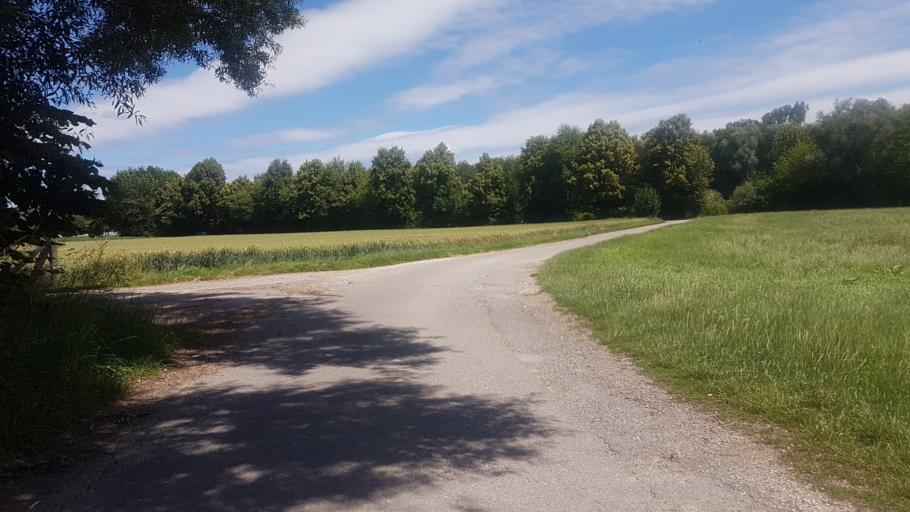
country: DE
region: Bavaria
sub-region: Swabia
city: Hochstadt an der Donau
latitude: 48.6063
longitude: 10.5761
